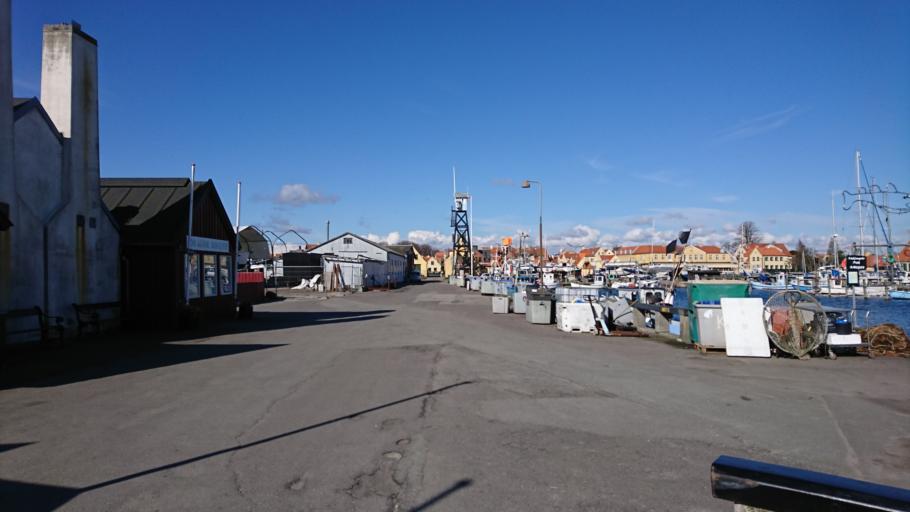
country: DK
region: Capital Region
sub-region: Dragor Kommune
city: Dragor
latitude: 55.5935
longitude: 12.6773
